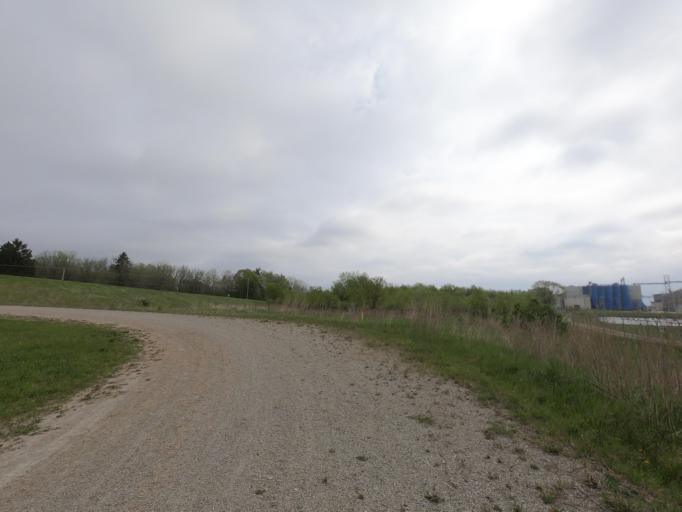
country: US
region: Wisconsin
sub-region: Jefferson County
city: Jefferson
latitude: 43.0392
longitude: -88.8013
